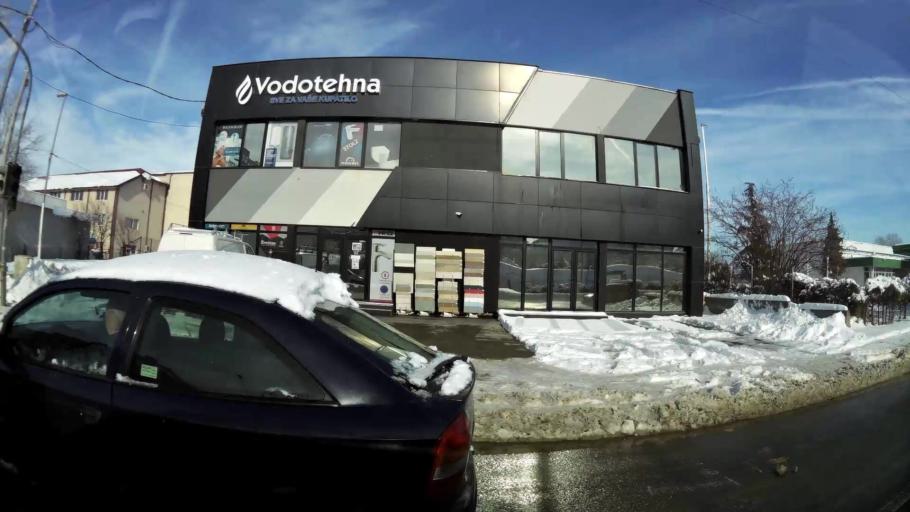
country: RS
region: Central Serbia
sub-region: Belgrade
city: Palilula
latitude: 44.8172
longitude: 20.5107
